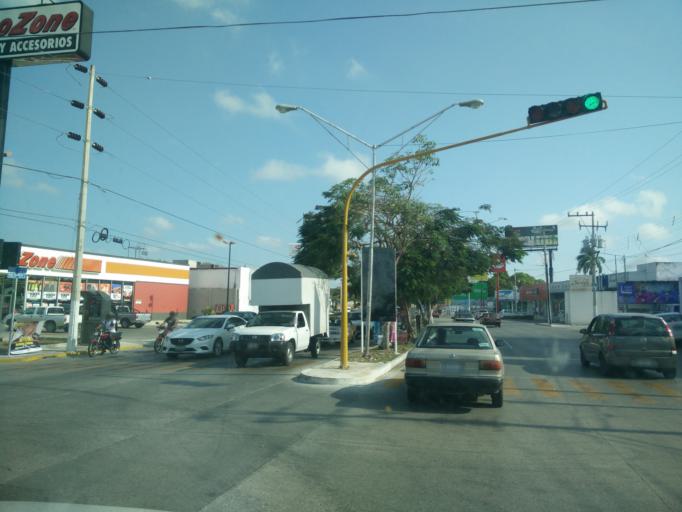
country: MX
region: Yucatan
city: Merida
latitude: 21.0111
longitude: -89.6135
